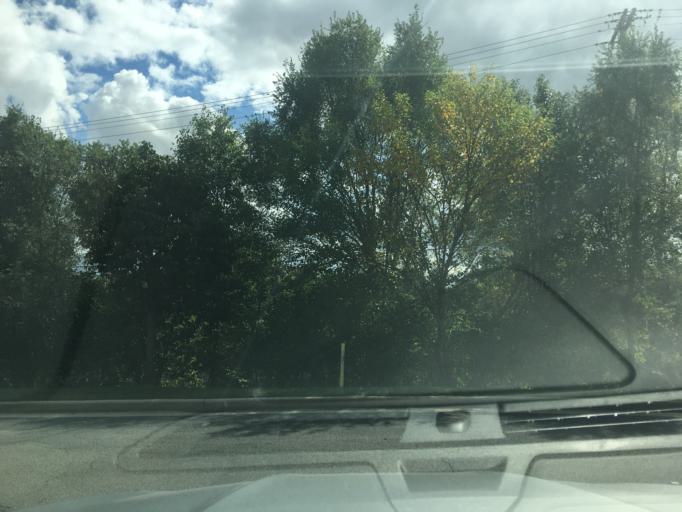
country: US
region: Indiana
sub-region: Tippecanoe County
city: West Lafayette
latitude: 40.4205
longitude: -86.9041
